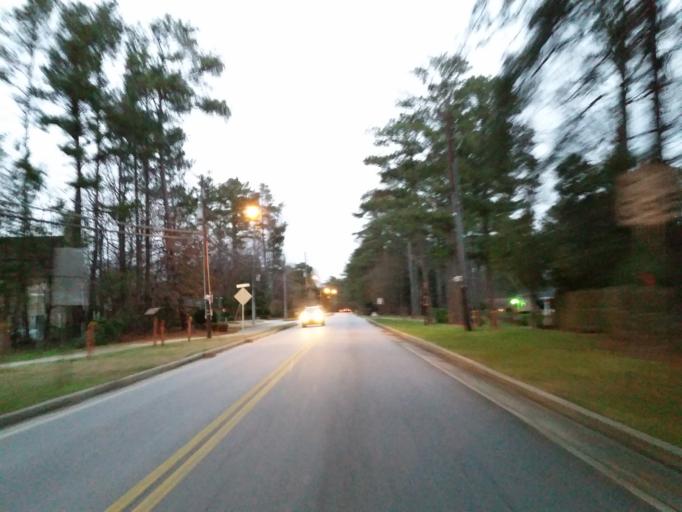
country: US
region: Georgia
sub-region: Cobb County
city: Mableton
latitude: 33.8554
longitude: -84.5526
